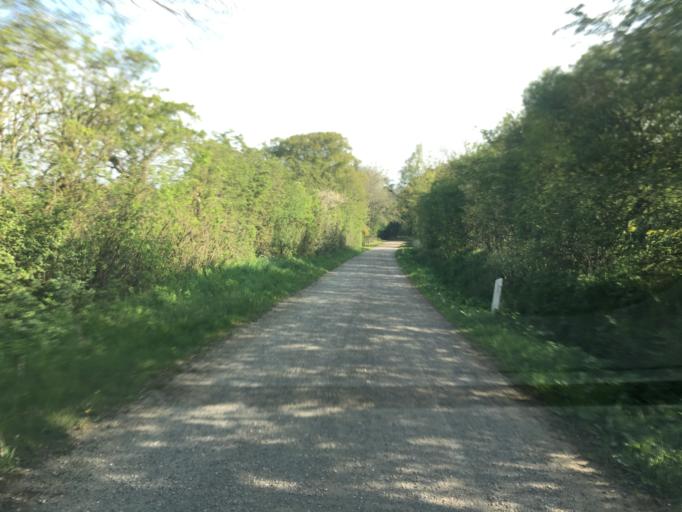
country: DK
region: South Denmark
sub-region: Haderslev Kommune
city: Vojens
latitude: 55.1803
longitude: 9.3875
